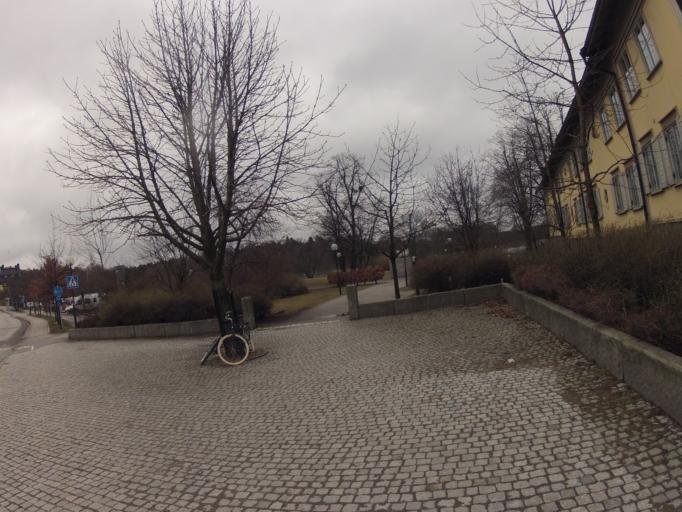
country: SE
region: Stockholm
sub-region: Stockholms Kommun
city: Stockholm
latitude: 59.3519
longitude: 18.0424
